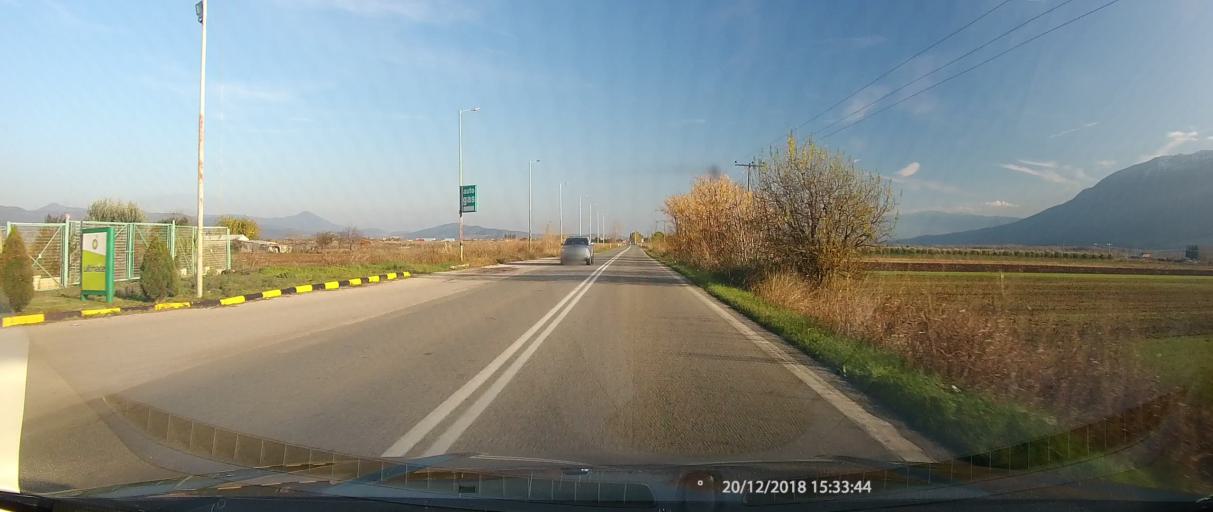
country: GR
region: Central Greece
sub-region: Nomos Fthiotidos
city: Lianokladhion
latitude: 38.9222
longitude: 22.2817
